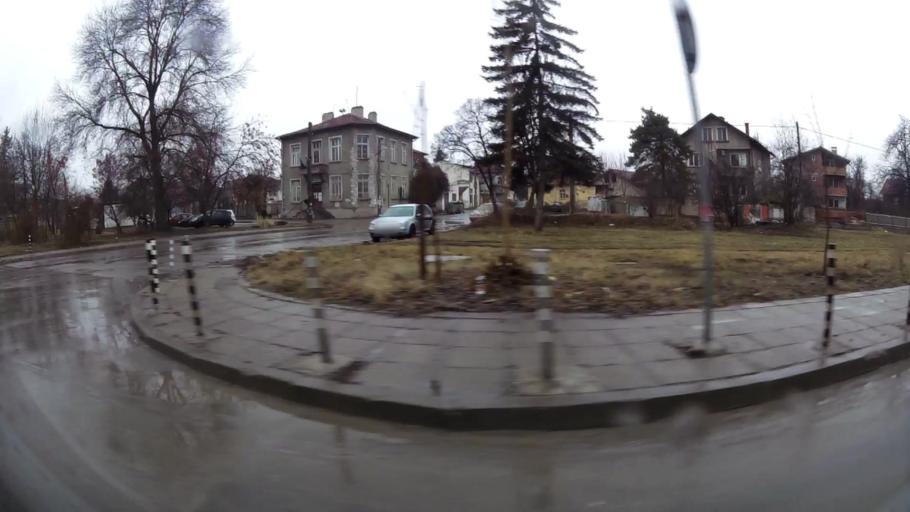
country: BG
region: Sofia-Capital
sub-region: Stolichna Obshtina
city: Sofia
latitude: 42.6289
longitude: 23.4081
